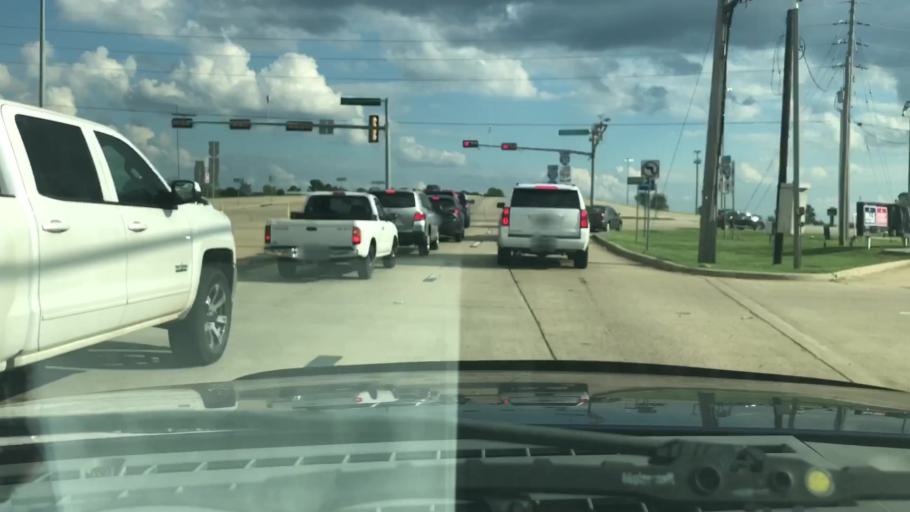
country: US
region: Arkansas
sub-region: Miller County
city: Texarkana
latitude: 33.4673
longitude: -94.0675
